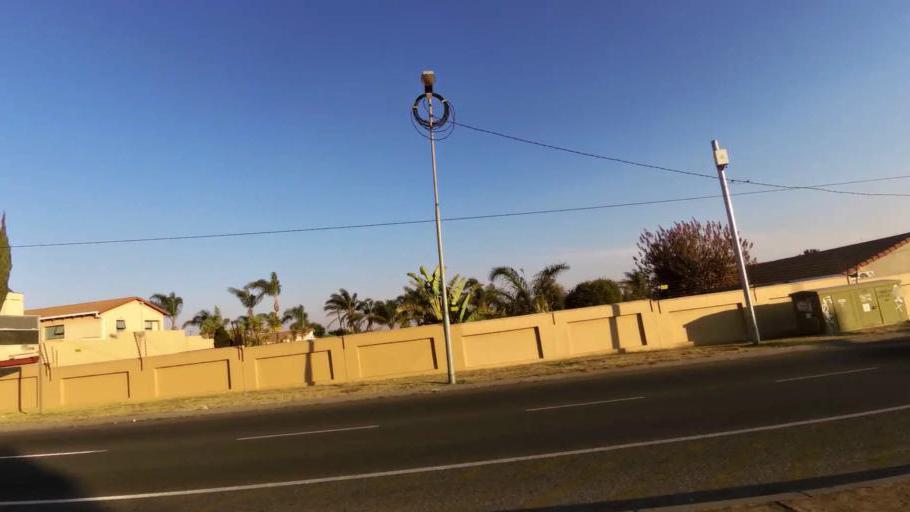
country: ZA
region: Gauteng
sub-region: City of Johannesburg Metropolitan Municipality
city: Roodepoort
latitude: -26.1639
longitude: 27.9524
